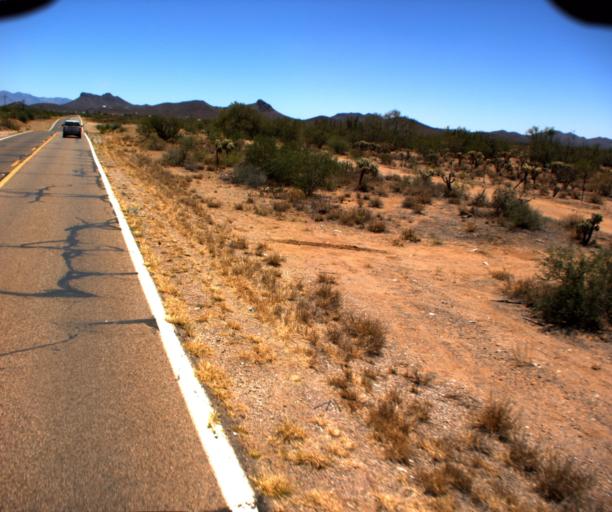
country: US
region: Arizona
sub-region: Pima County
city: Sells
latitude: 31.9310
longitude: -111.9078
